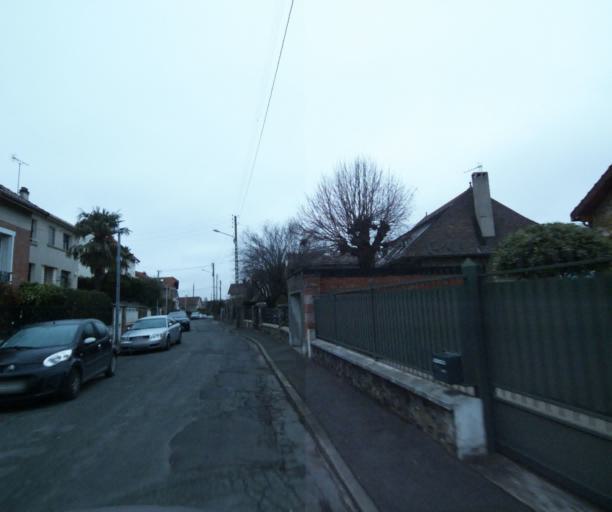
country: FR
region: Ile-de-France
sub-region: Departement du Val-de-Marne
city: Ablon-sur-Seine
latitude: 48.7267
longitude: 2.4126
